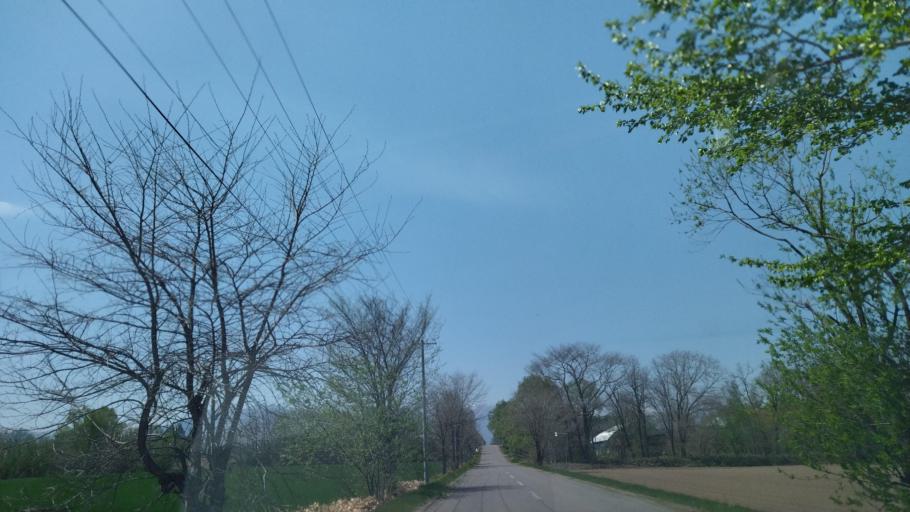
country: JP
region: Hokkaido
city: Obihiro
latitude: 42.8943
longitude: 143.0286
